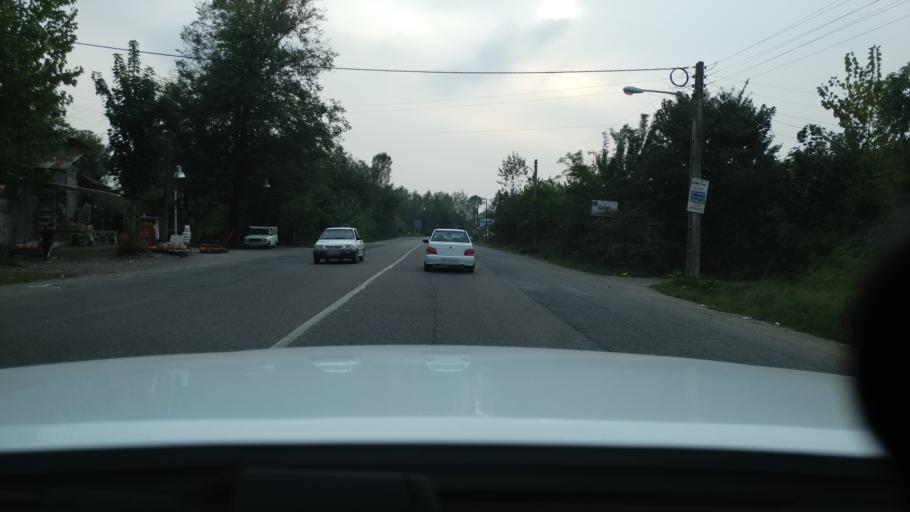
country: IR
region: Gilan
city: Siahkal
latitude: 37.1781
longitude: 49.8966
